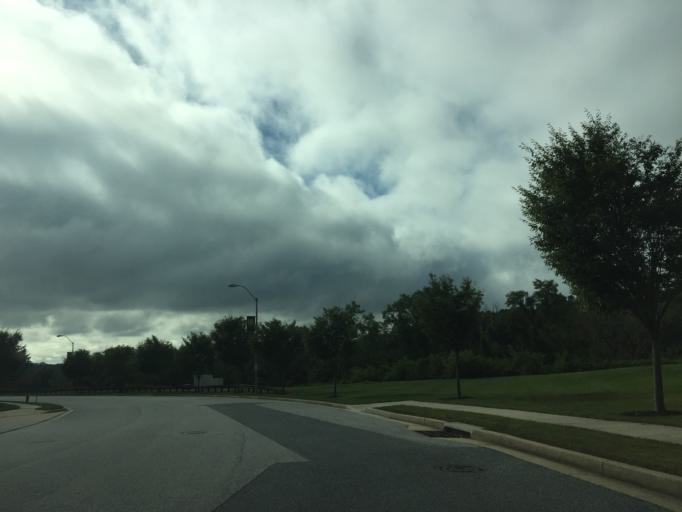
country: US
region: Maryland
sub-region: Baltimore County
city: Lutherville
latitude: 39.3794
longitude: -76.6573
